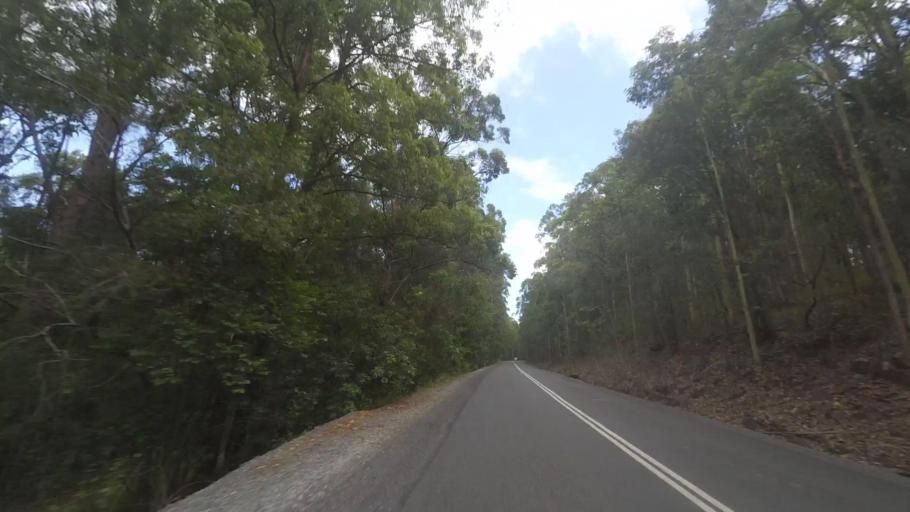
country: AU
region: New South Wales
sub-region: Great Lakes
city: Bulahdelah
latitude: -32.3895
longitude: 152.2429
